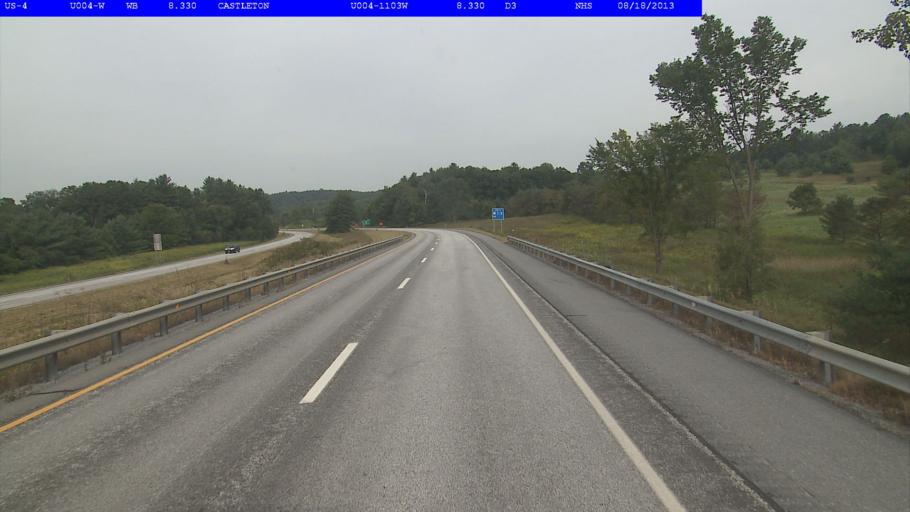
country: US
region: Vermont
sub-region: Rutland County
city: Castleton
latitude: 43.6161
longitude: -73.1536
